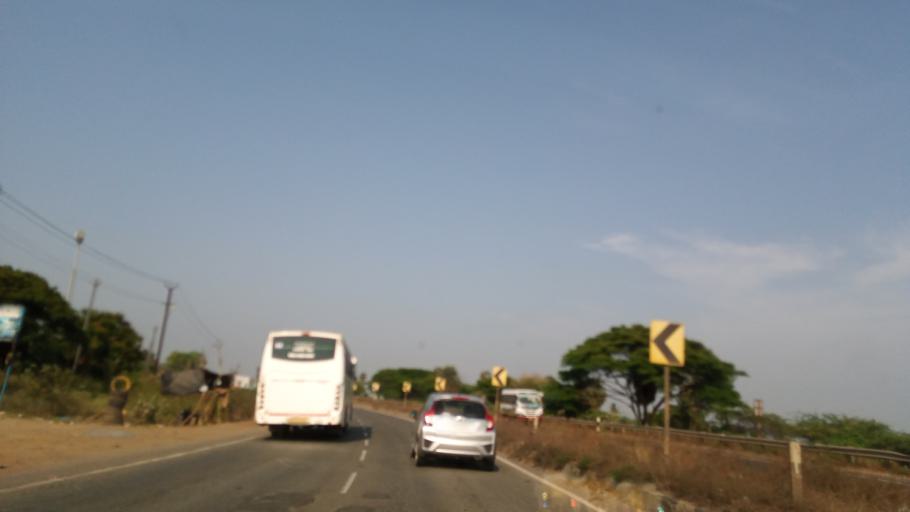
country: IN
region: Tamil Nadu
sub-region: Kancheepuram
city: Sriperumbudur
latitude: 12.9645
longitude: 79.9506
